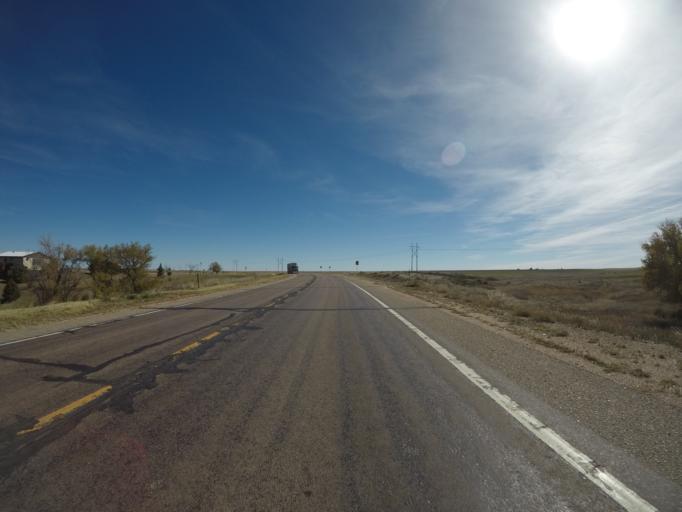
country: US
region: Colorado
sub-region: Yuma County
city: Yuma
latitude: 39.6562
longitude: -102.8441
